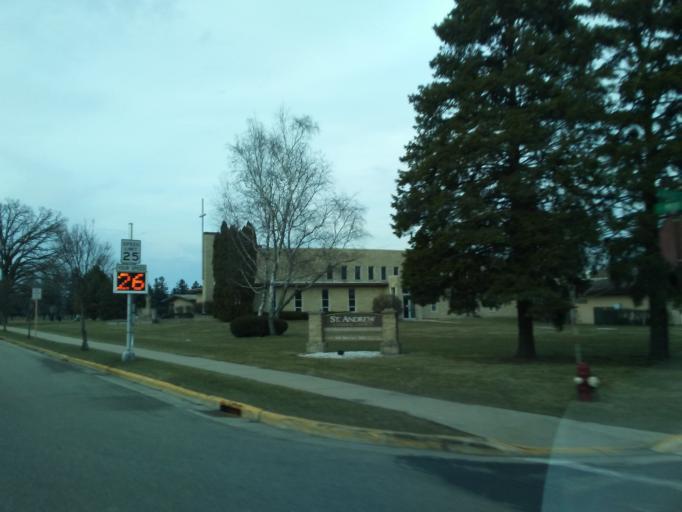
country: US
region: Wisconsin
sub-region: Dane County
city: Verona
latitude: 42.9938
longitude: -89.5336
